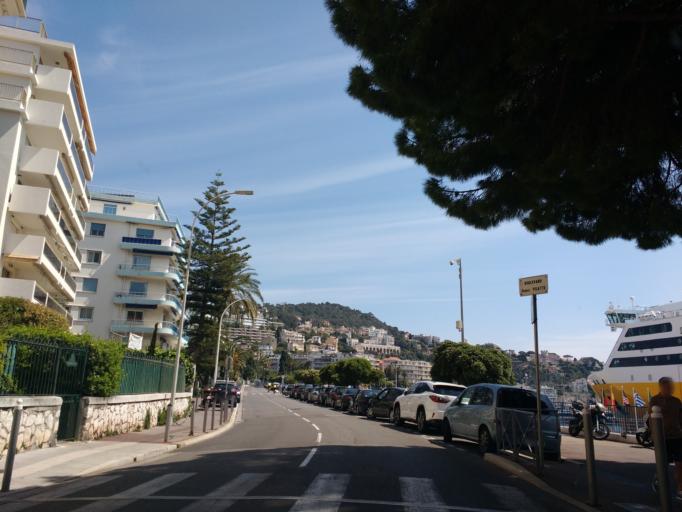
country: FR
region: Provence-Alpes-Cote d'Azur
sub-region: Departement des Alpes-Maritimes
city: Nice
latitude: 43.6945
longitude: 7.2867
